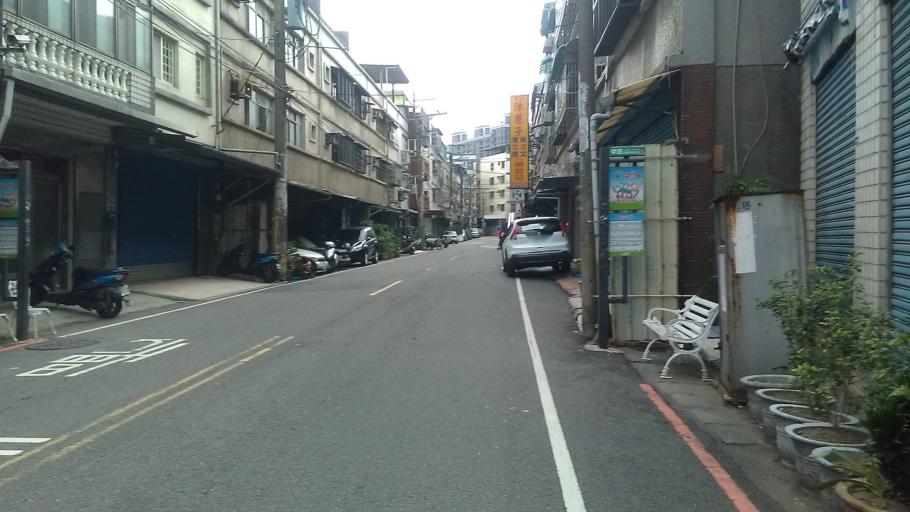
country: TW
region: Taiwan
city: Taoyuan City
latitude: 24.9499
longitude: 121.2621
